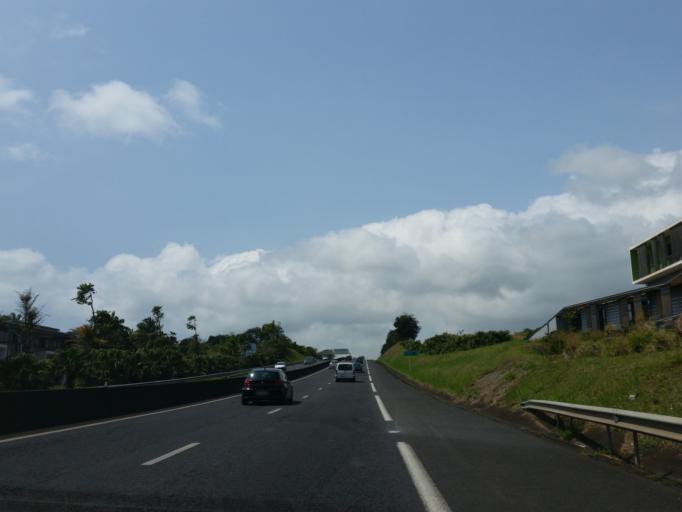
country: RE
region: Reunion
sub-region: Reunion
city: Sainte-Marie
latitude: -20.9002
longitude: 55.5265
